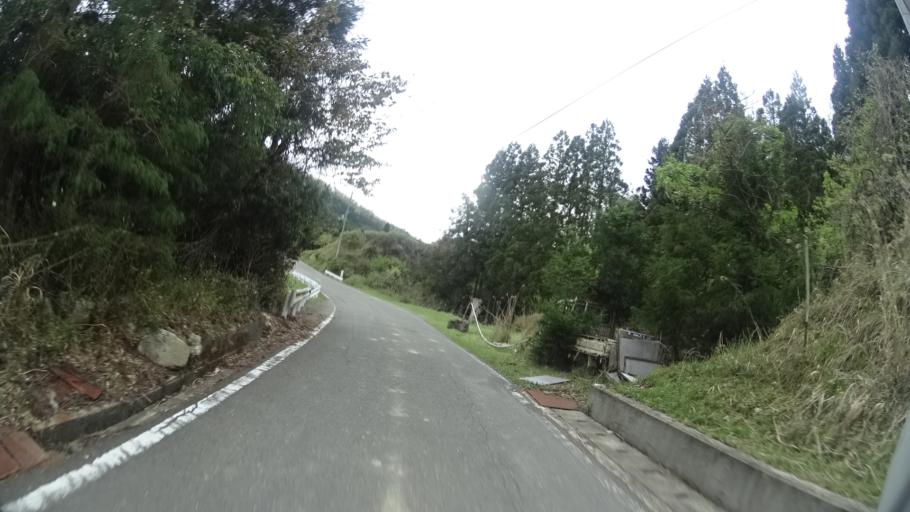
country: JP
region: Kyoto
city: Ayabe
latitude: 35.2196
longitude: 135.4701
